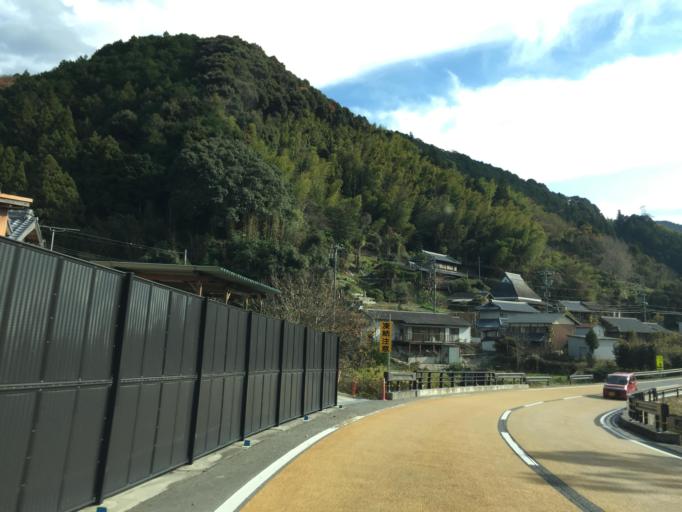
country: JP
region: Wakayama
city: Iwade
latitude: 34.1430
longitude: 135.3847
